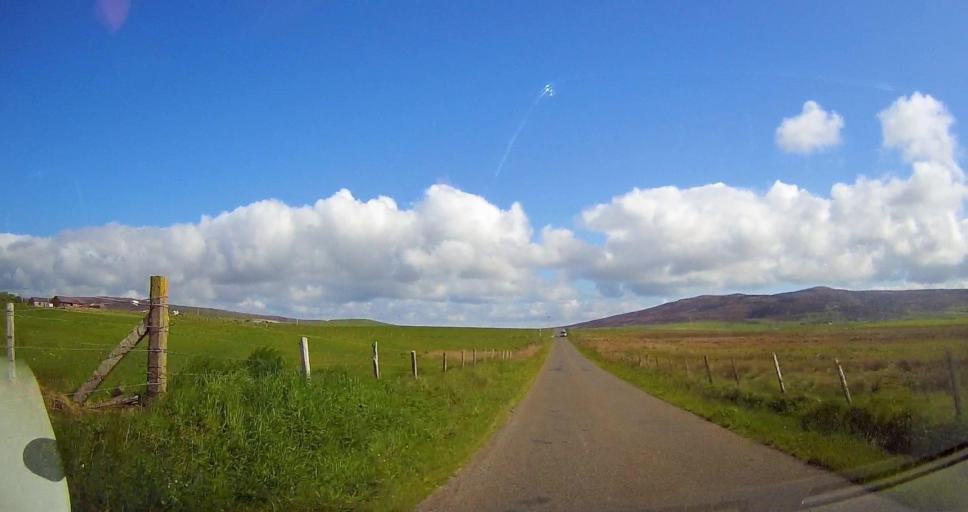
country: GB
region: Scotland
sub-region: Orkney Islands
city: Stromness
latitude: 58.9928
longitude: -3.1573
